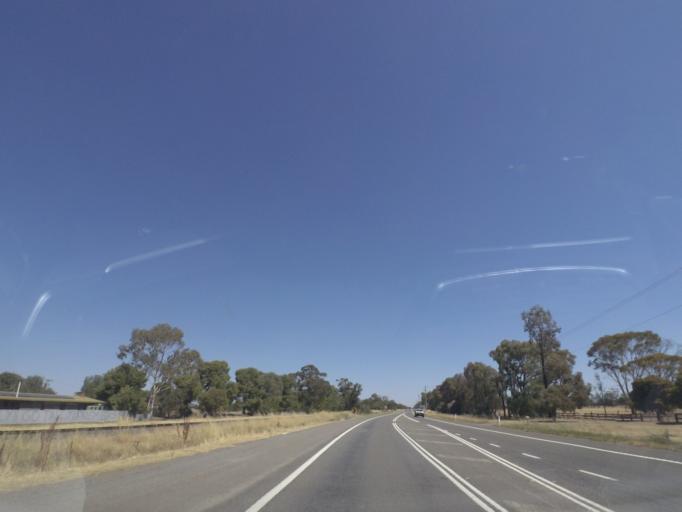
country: AU
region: Victoria
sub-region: Greater Shepparton
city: Shepparton
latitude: -36.2398
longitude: 145.4318
